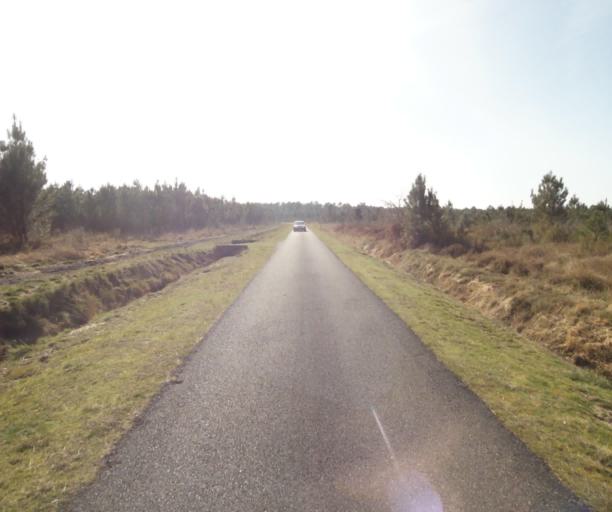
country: FR
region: Aquitaine
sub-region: Departement des Landes
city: Roquefort
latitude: 44.2112
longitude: -0.2535
